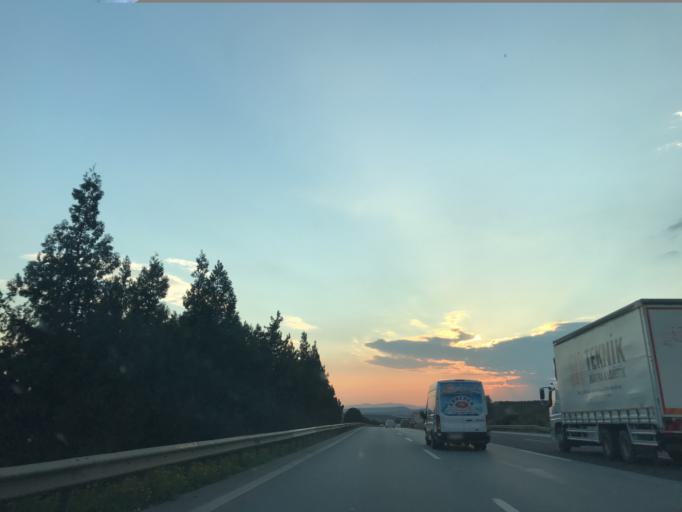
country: TR
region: Mersin
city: Yenice
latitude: 37.0164
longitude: 35.0023
